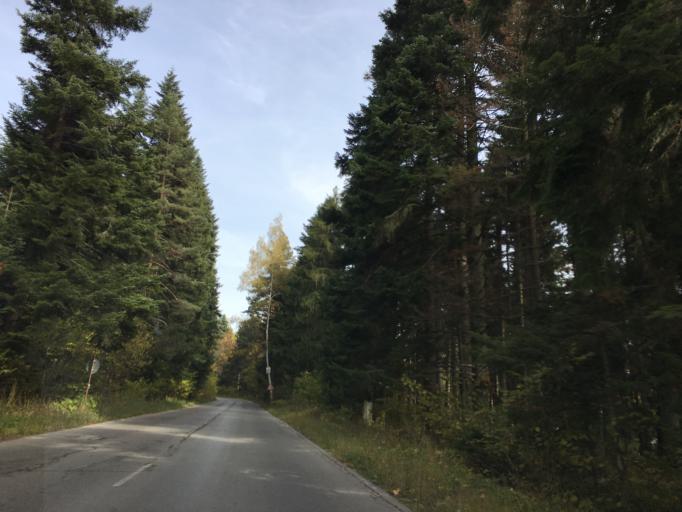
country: BG
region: Sofiya
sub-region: Obshtina Samokov
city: Samokov
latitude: 42.2753
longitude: 23.6225
